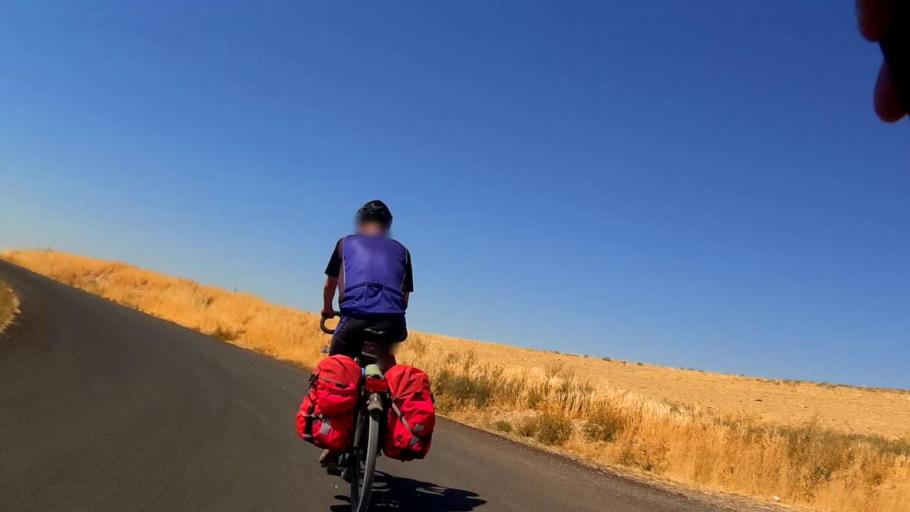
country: US
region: Idaho
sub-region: Madison County
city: Rexburg
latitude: 43.7183
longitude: -111.7441
